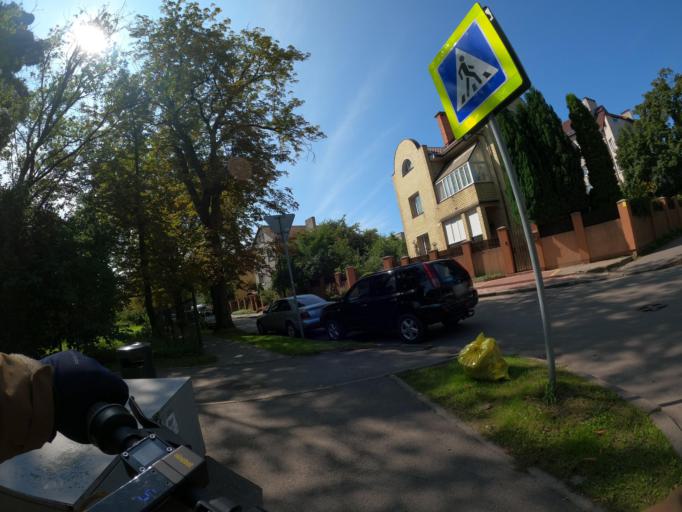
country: RU
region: Kaliningrad
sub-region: Gorod Kaliningrad
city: Kaliningrad
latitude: 54.7349
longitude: 20.5276
